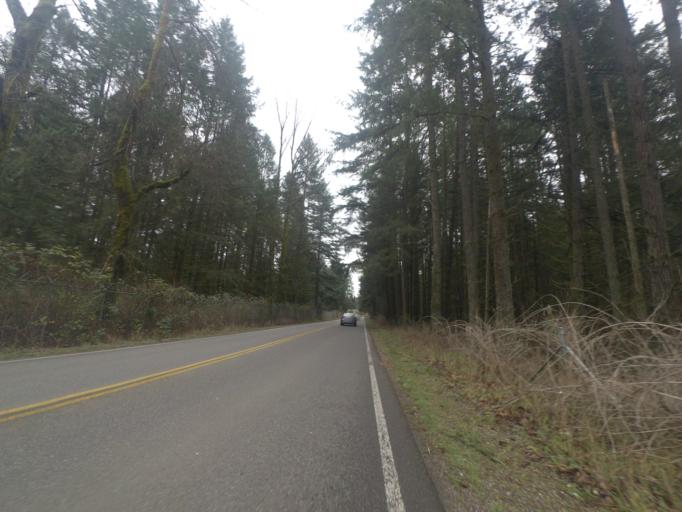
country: US
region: Washington
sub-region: Pierce County
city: McChord Air Force Base
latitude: 47.1186
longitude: -122.5049
